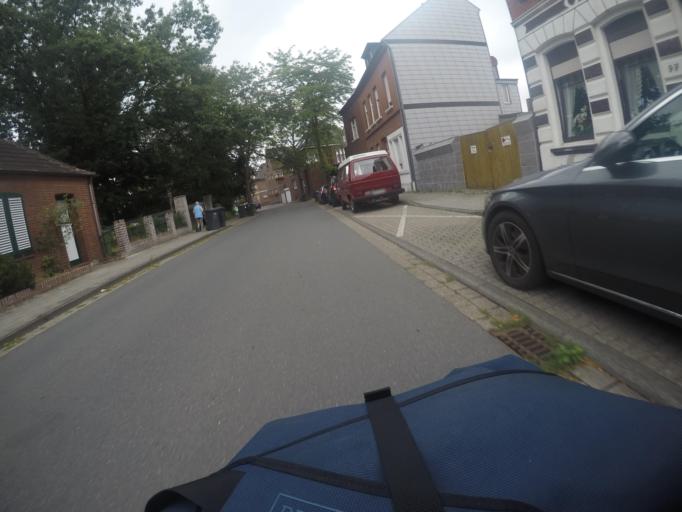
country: DE
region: North Rhine-Westphalia
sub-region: Regierungsbezirk Dusseldorf
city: Kevelaer
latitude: 51.5844
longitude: 6.2476
